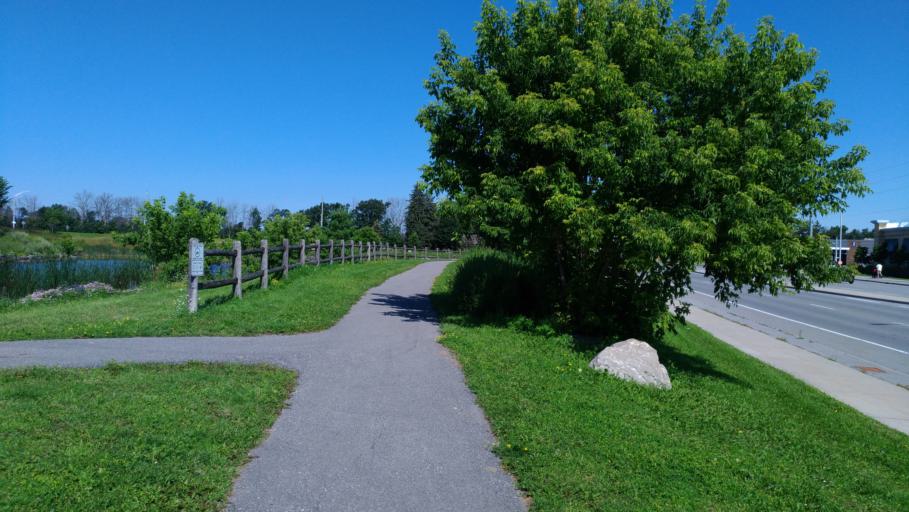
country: CA
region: Ontario
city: Bells Corners
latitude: 45.3572
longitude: -75.9356
